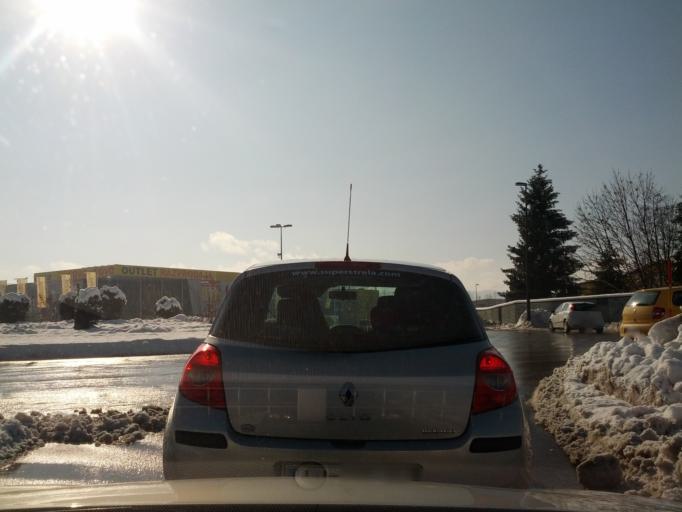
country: SI
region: Skofljica
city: Lavrica
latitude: 46.0215
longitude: 14.5343
